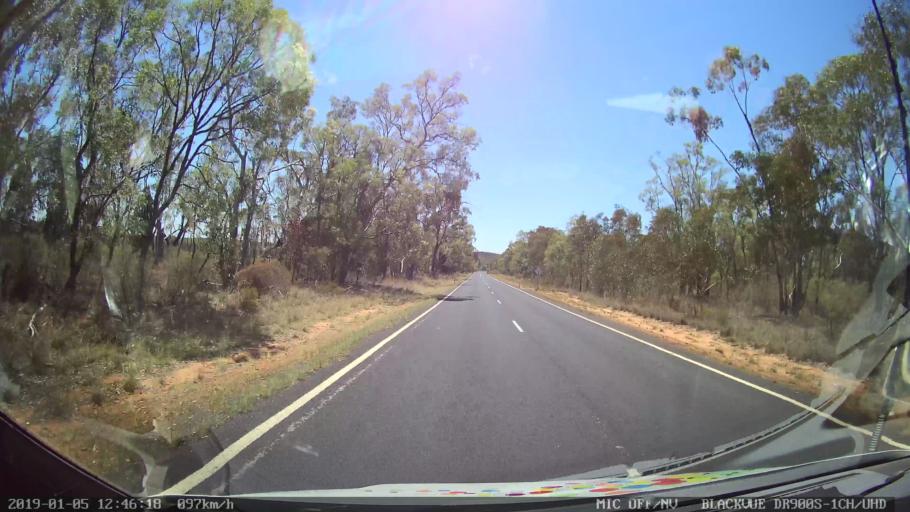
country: AU
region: New South Wales
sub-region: Warrumbungle Shire
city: Coonabarabran
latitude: -31.1194
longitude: 149.5607
